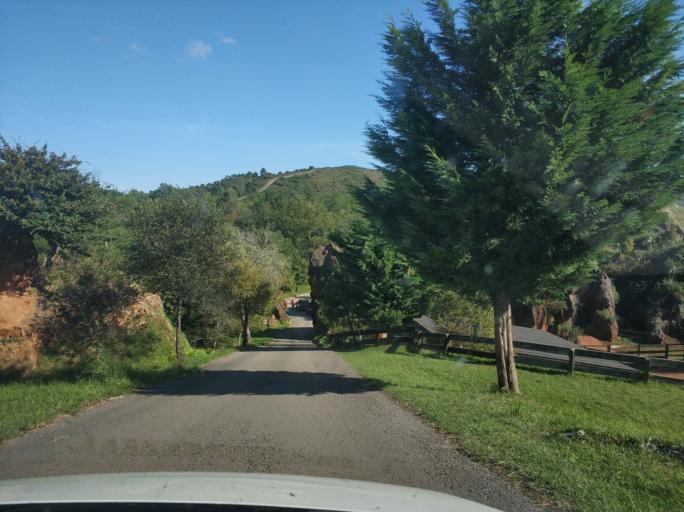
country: ES
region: Cantabria
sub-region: Provincia de Cantabria
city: Penagos
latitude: 43.3508
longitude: -3.8457
